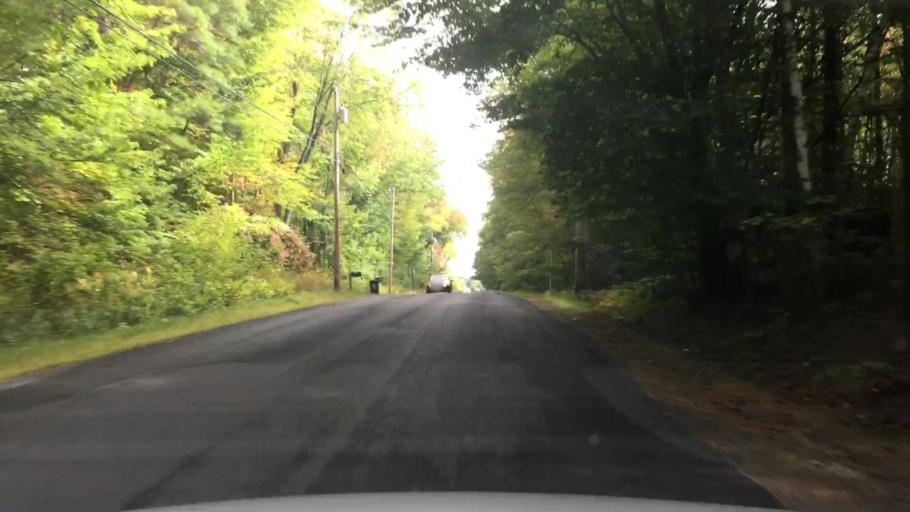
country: US
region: Maine
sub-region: Androscoggin County
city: Lisbon Falls
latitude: 43.9686
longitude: -70.0702
